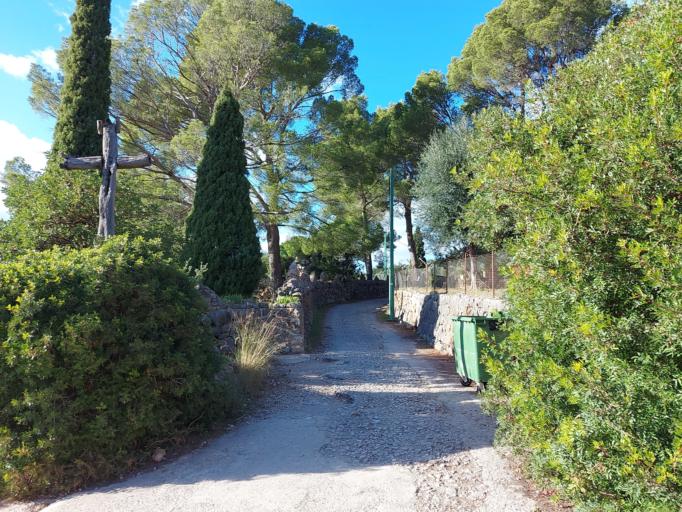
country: ES
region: Balearic Islands
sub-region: Illes Balears
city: Soller
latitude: 39.7782
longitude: 2.7220
